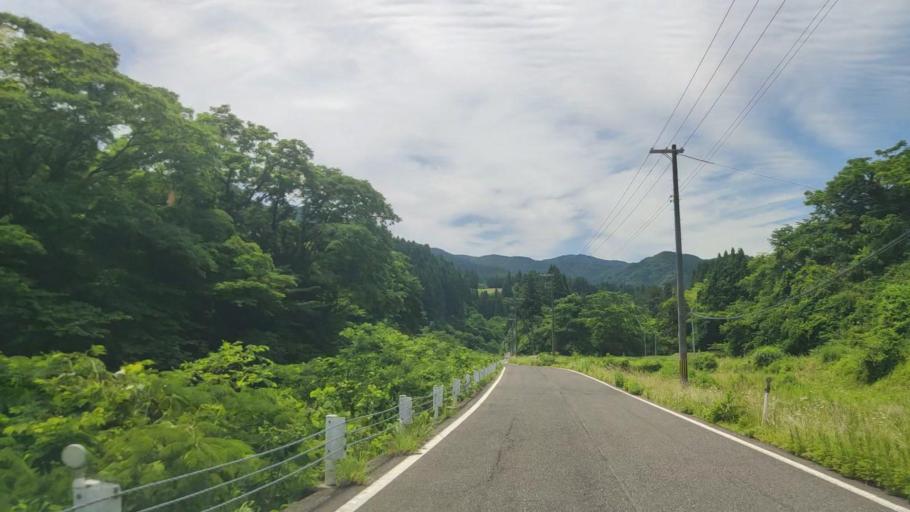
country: JP
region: Tottori
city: Tottori
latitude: 35.4278
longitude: 134.5283
